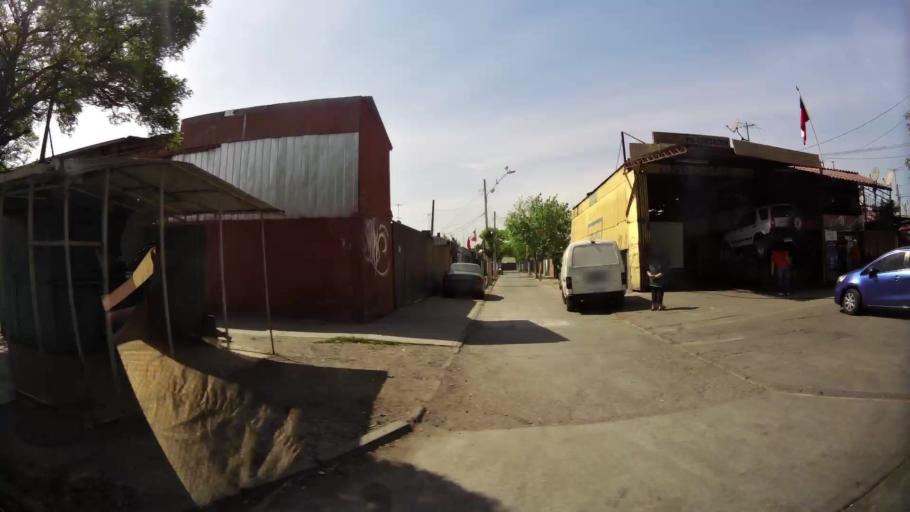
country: CL
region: Santiago Metropolitan
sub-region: Provincia de Santiago
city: Lo Prado
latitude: -33.4332
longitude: -70.7625
